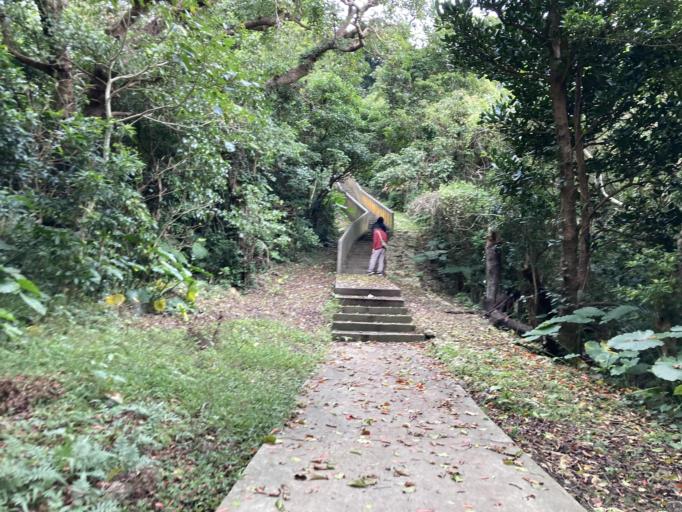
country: JP
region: Okinawa
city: Chatan
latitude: 26.2848
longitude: 127.8065
